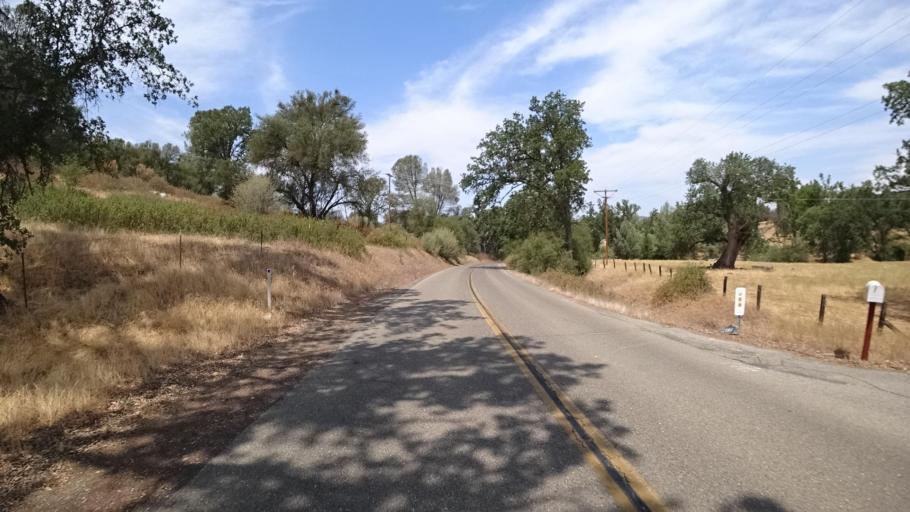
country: US
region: California
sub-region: Mariposa County
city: Mariposa
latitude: 37.4101
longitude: -119.8571
